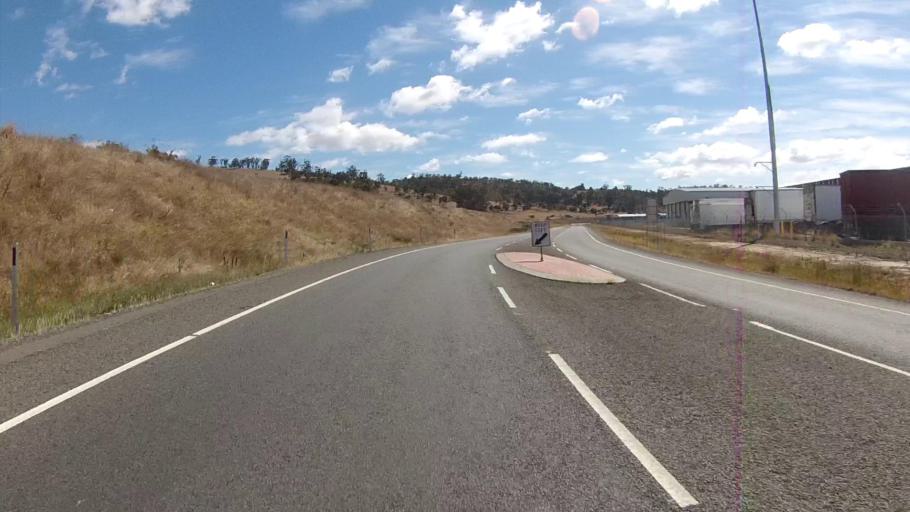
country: AU
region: Tasmania
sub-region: Brighton
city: Bridgewater
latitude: -42.7175
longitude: 147.2256
